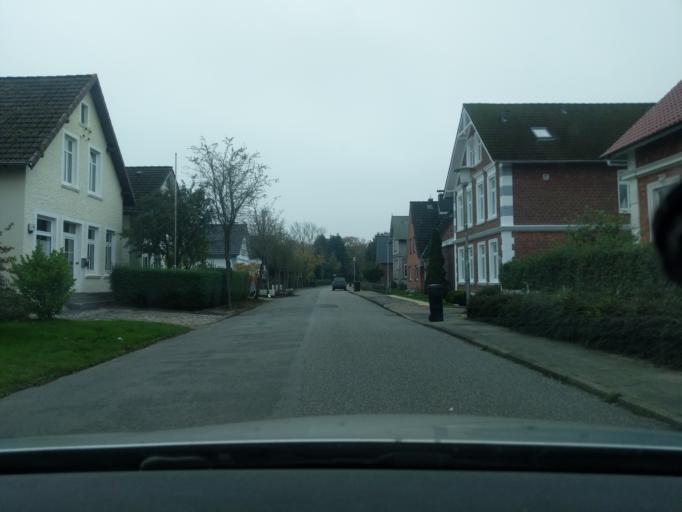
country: DE
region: Lower Saxony
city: Wanna
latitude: 53.8264
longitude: 8.7758
